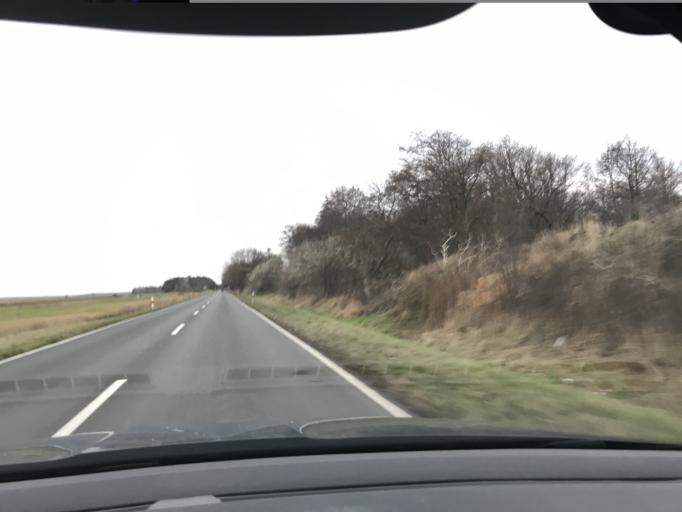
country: DE
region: Mecklenburg-Vorpommern
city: Ostseebad Dierhagen
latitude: 54.3402
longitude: 12.3801
